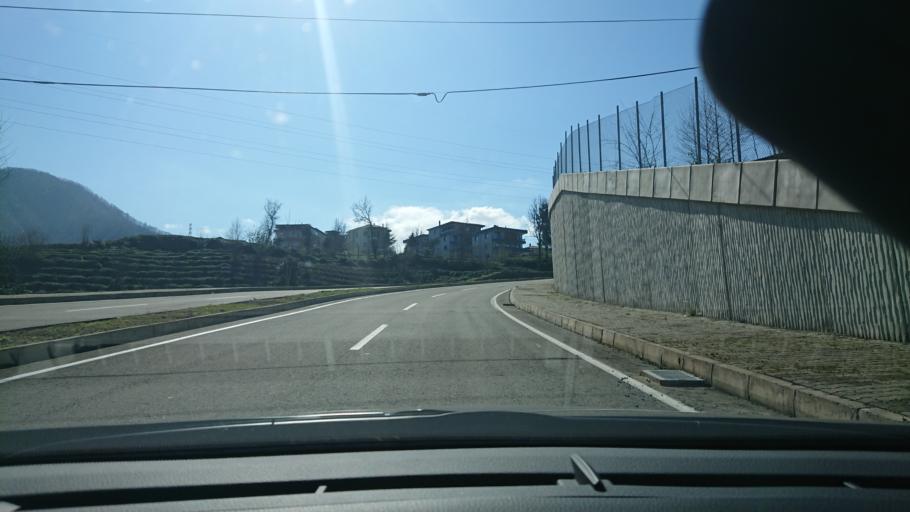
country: TR
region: Rize
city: Rize
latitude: 40.9996
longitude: 40.4893
